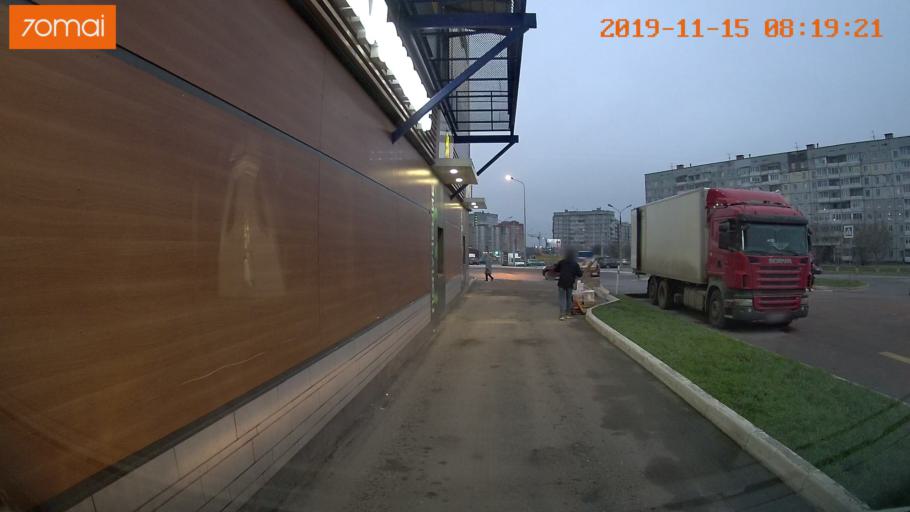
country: RU
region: Vologda
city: Cherepovets
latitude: 59.0930
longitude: 37.9182
